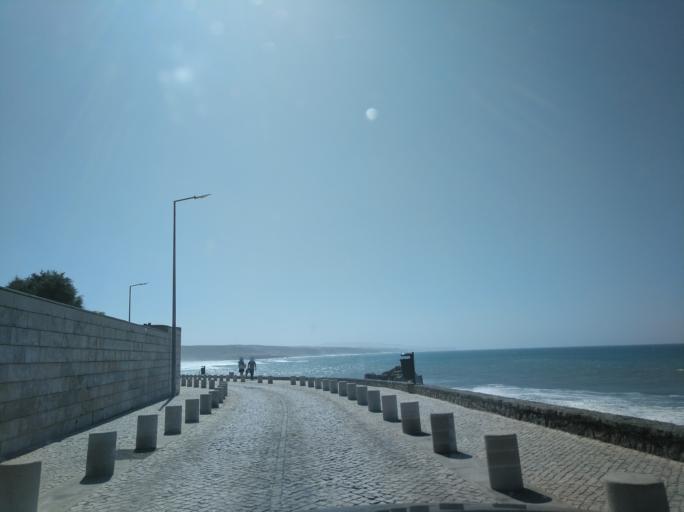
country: PT
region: Lisbon
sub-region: Mafra
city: Ericeira
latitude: 38.9611
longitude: -9.4195
